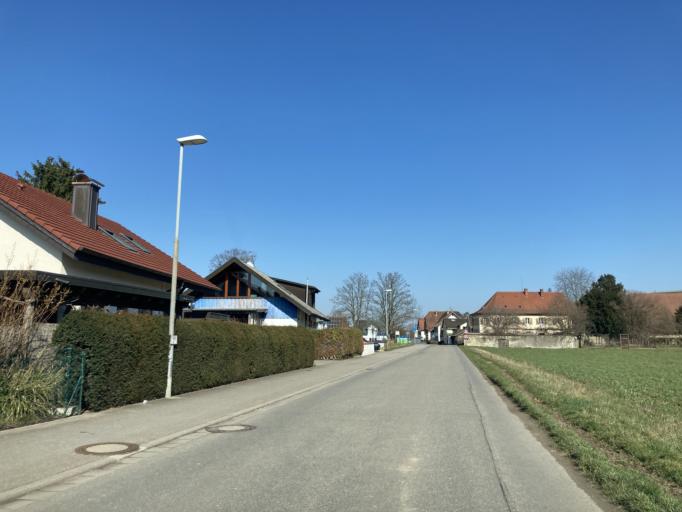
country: DE
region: Baden-Wuerttemberg
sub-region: Freiburg Region
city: Buggingen
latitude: 47.8562
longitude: 7.6421
